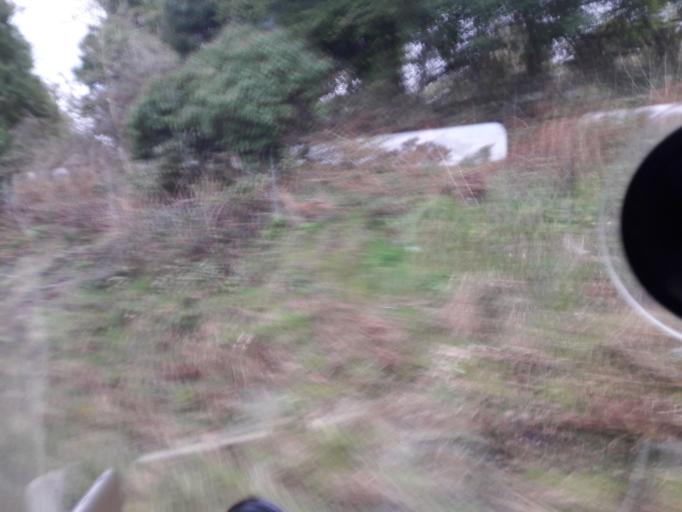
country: IE
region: Leinster
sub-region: An Iarmhi
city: Rathwire
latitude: 53.4951
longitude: -7.1718
